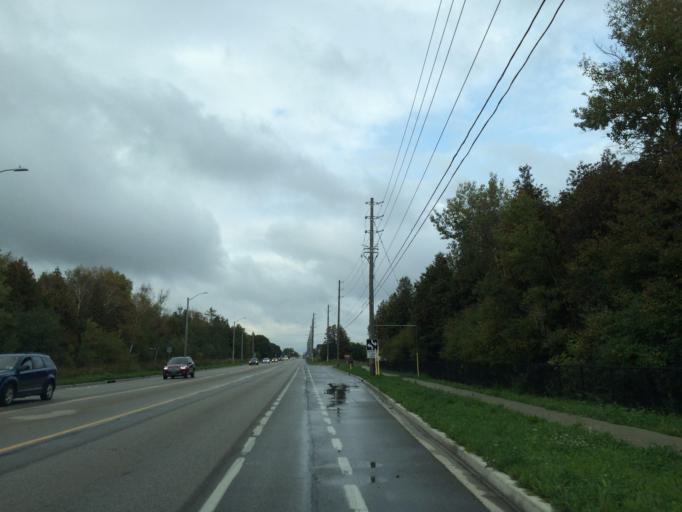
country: CA
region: Ontario
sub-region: Wellington County
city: Guelph
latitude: 43.5278
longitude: -80.1909
